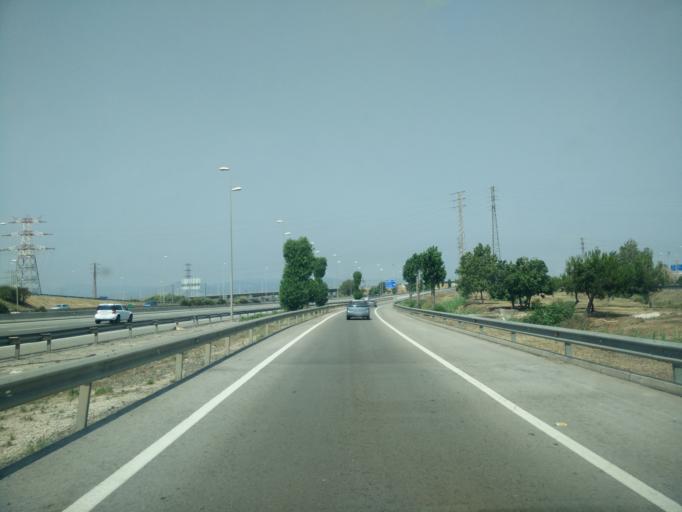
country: ES
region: Catalonia
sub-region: Provincia de Barcelona
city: El Prat de Llobregat
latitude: 41.3413
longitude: 2.0988
